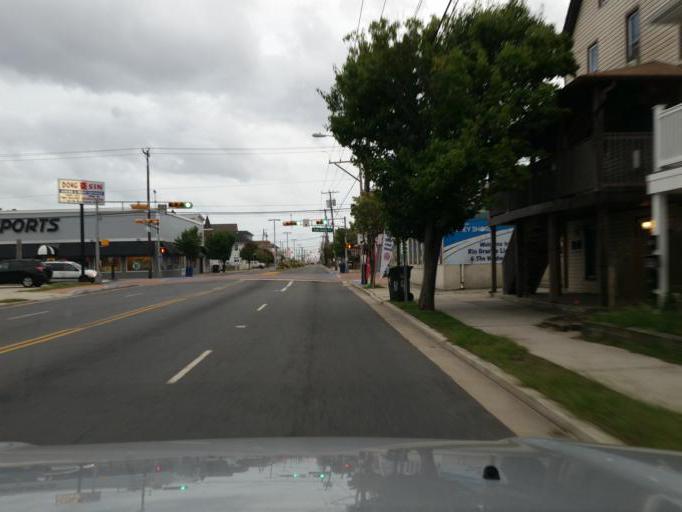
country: US
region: New Jersey
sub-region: Cape May County
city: Wildwood
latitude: 38.9845
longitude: -74.8253
